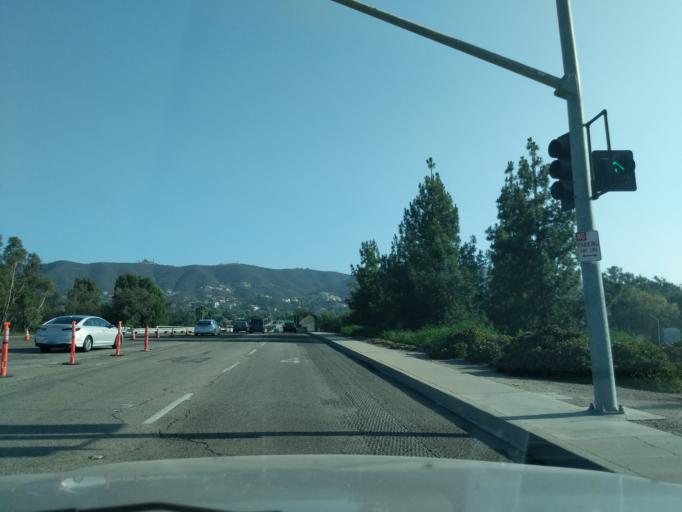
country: US
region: California
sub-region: Ventura County
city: Casa Conejo
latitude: 34.1854
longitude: -118.9113
